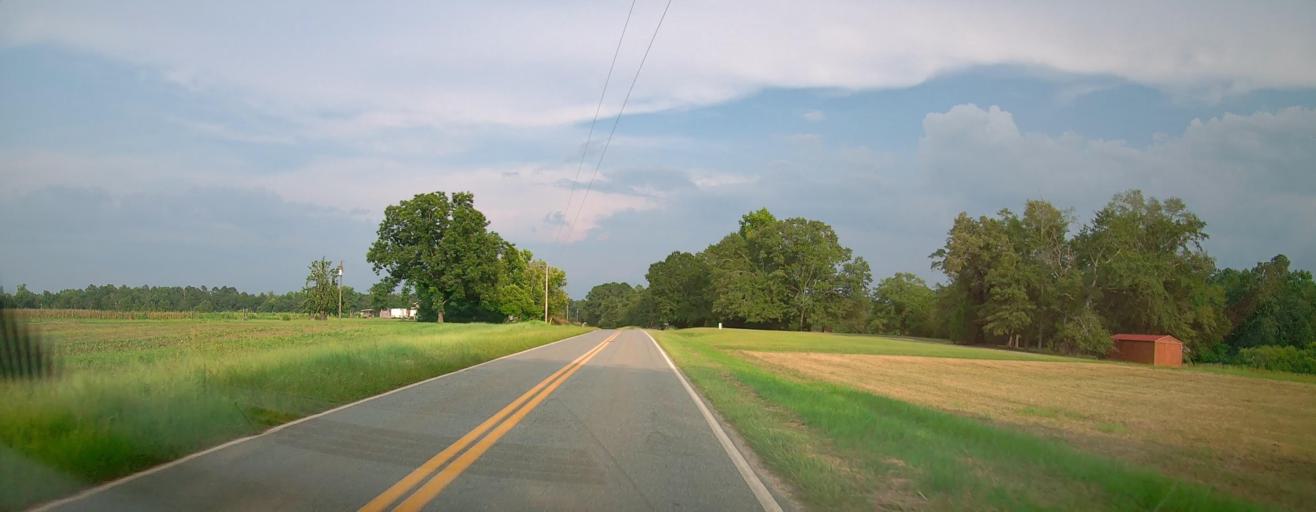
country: US
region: Georgia
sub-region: Laurens County
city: Dublin
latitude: 32.4820
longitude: -82.9662
